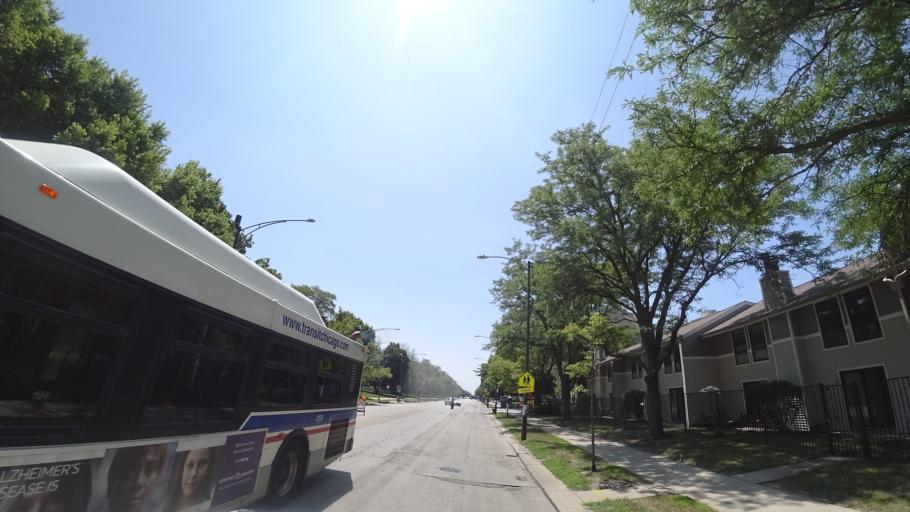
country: US
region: Illinois
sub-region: Cook County
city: Chicago
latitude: 41.7835
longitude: -87.5866
